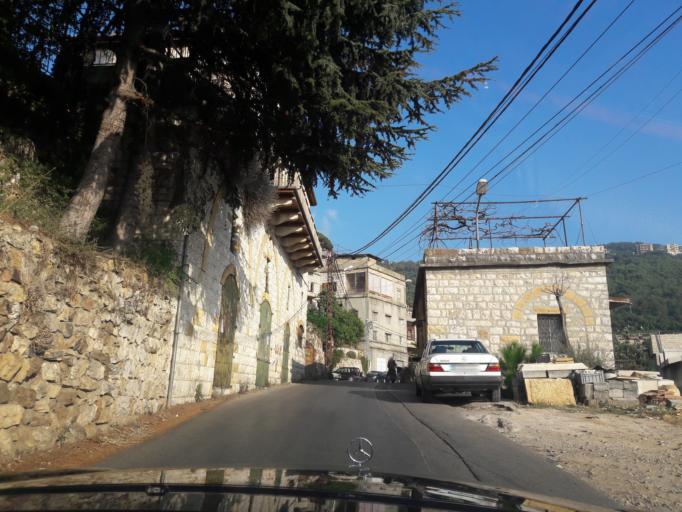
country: LB
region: Mont-Liban
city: Djounie
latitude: 33.9271
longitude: 35.6718
